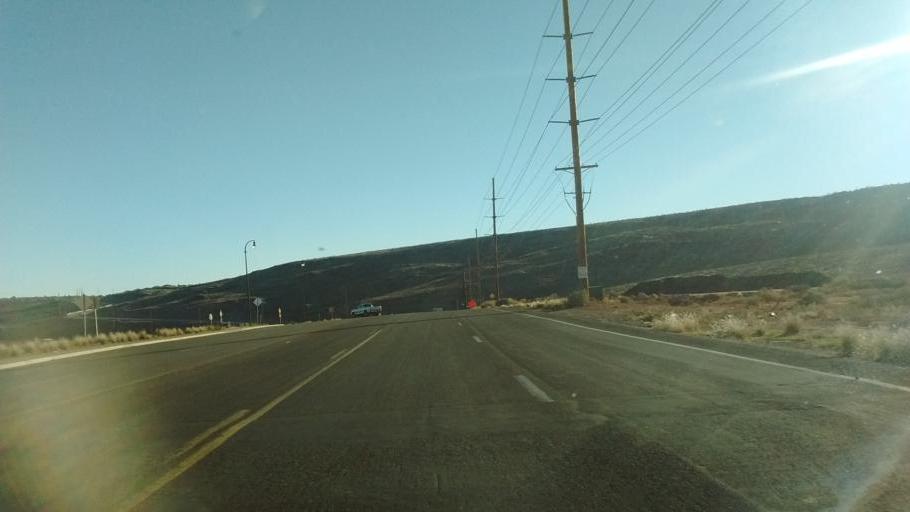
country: US
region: Utah
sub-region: Washington County
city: Washington
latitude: 37.1312
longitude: -113.4866
